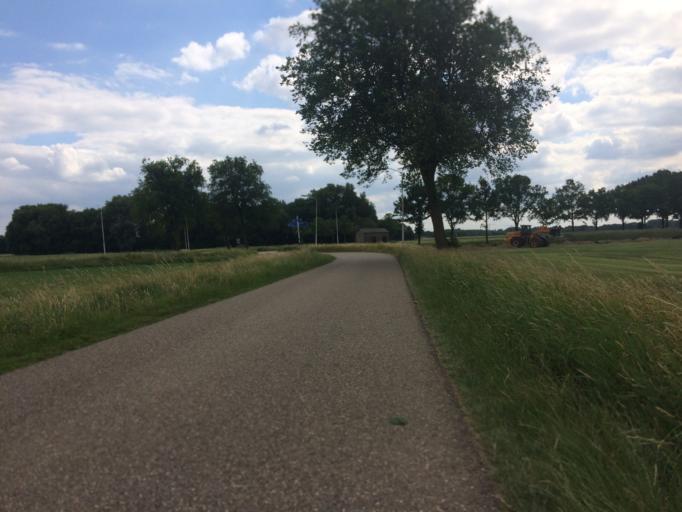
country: NL
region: Gelderland
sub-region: Gemeente Zaltbommel
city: Nederhemert-Noord
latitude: 51.7253
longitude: 5.2098
